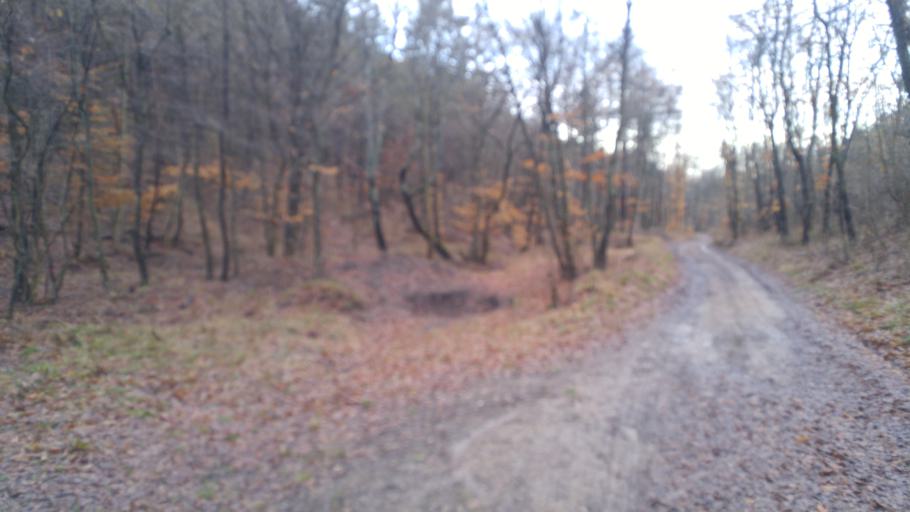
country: HU
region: Zala
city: Vonyarcvashegy
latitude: 46.7800
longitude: 17.3102
